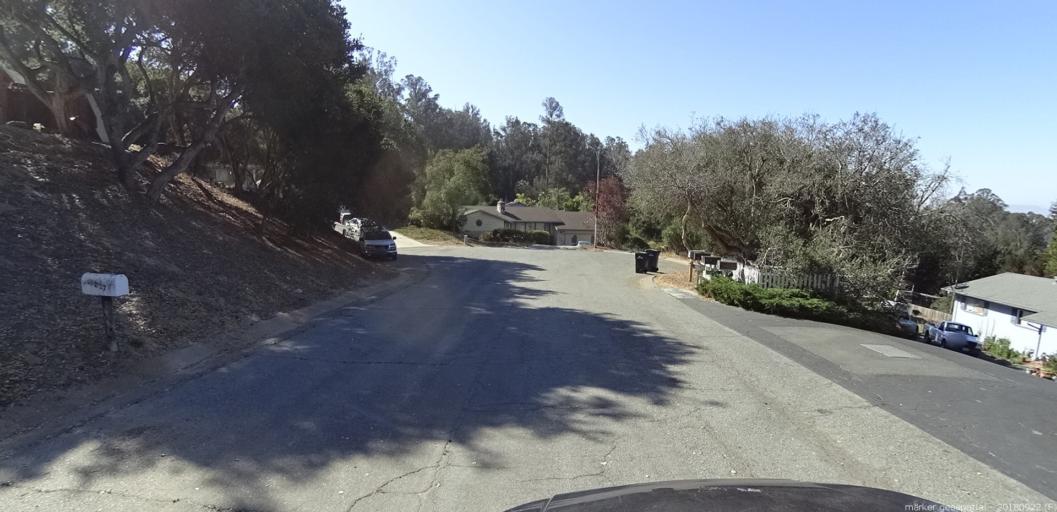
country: US
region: California
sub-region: Monterey County
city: Prunedale
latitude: 36.8130
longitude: -121.6537
